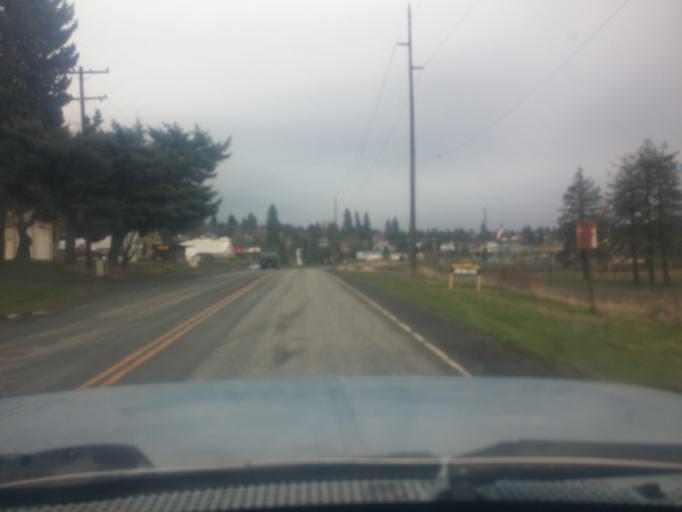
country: US
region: Idaho
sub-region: Latah County
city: Moscow
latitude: 46.9280
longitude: -116.9067
